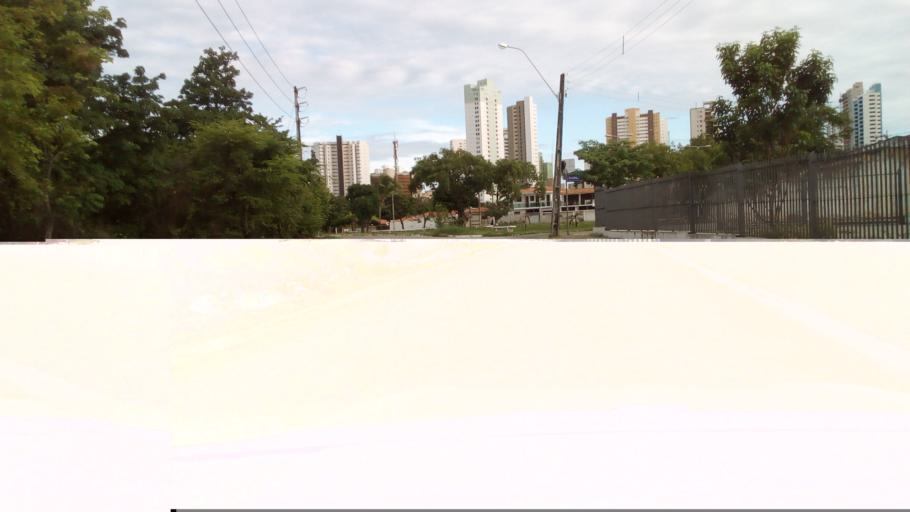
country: BR
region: Paraiba
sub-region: Joao Pessoa
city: Joao Pessoa
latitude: -7.1100
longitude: -34.8395
